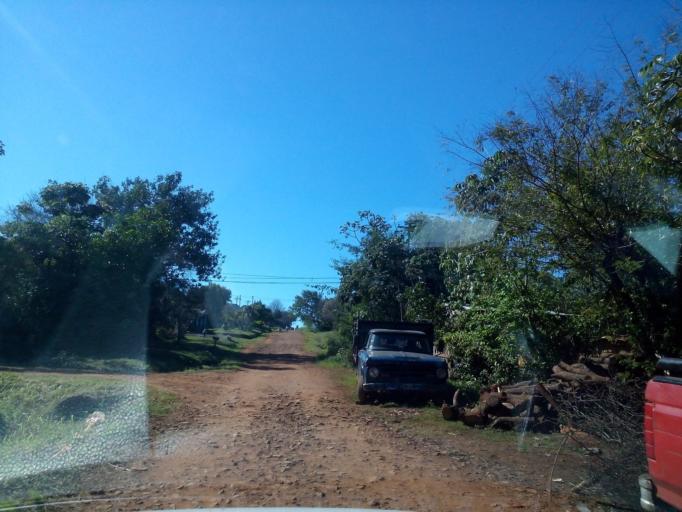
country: AR
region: Misiones
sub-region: Departamento de Capital
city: Posadas
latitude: -27.3789
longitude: -55.9469
